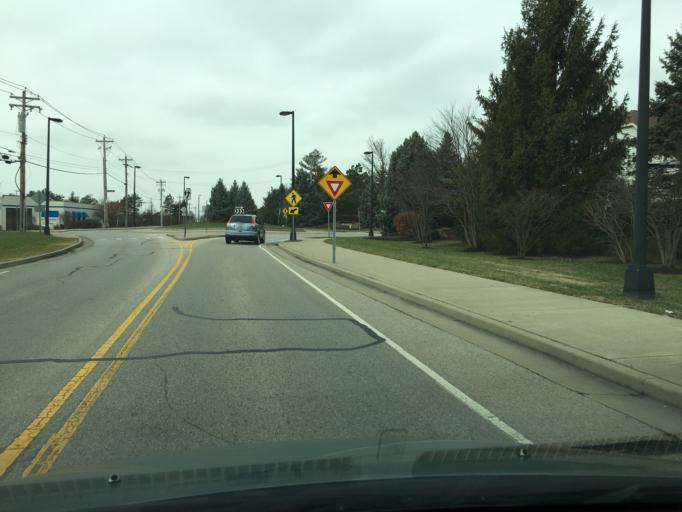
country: US
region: Ohio
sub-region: Butler County
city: Beckett Ridge
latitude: 39.3307
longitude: -84.4270
